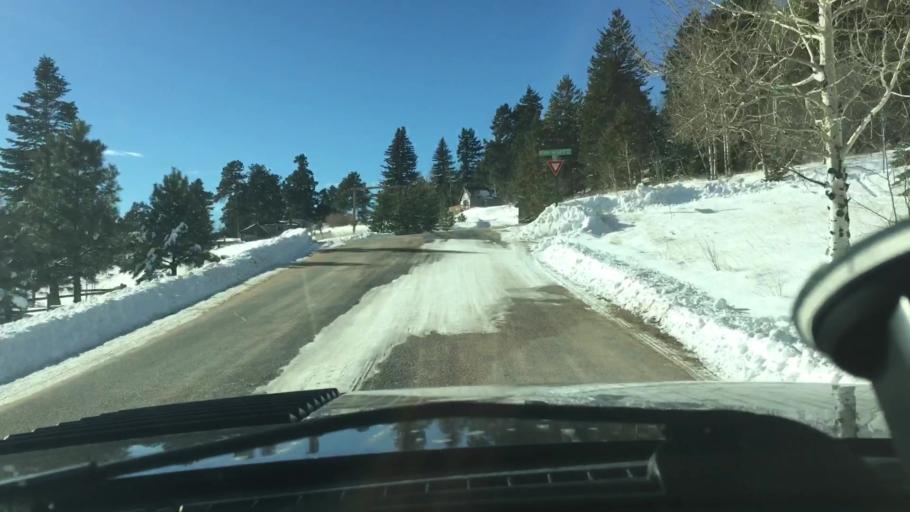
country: US
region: Colorado
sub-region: Jefferson County
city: Indian Hills
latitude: 39.5632
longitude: -105.2531
